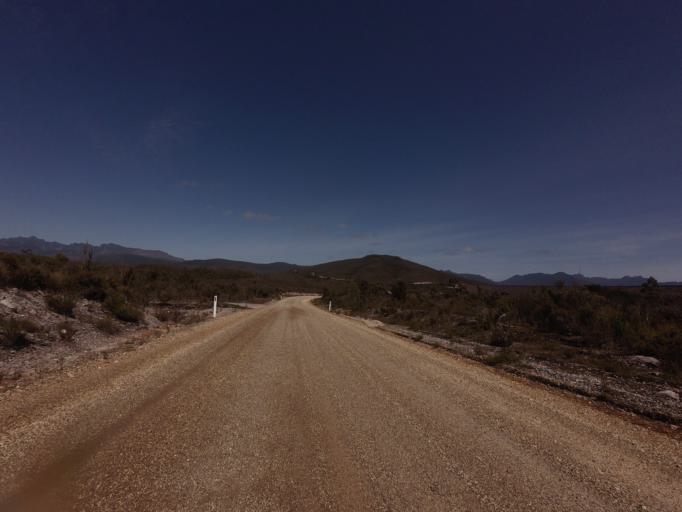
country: AU
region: Tasmania
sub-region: Huon Valley
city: Geeveston
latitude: -43.0320
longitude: 146.3034
